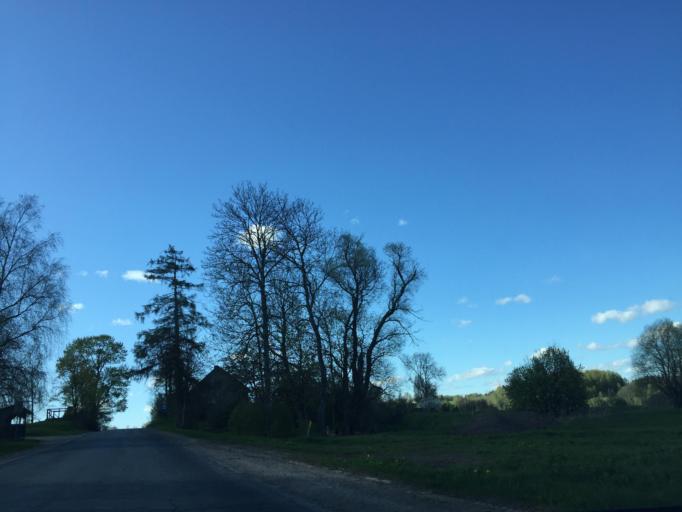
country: LV
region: Madonas Rajons
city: Madona
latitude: 56.8240
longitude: 25.9969
